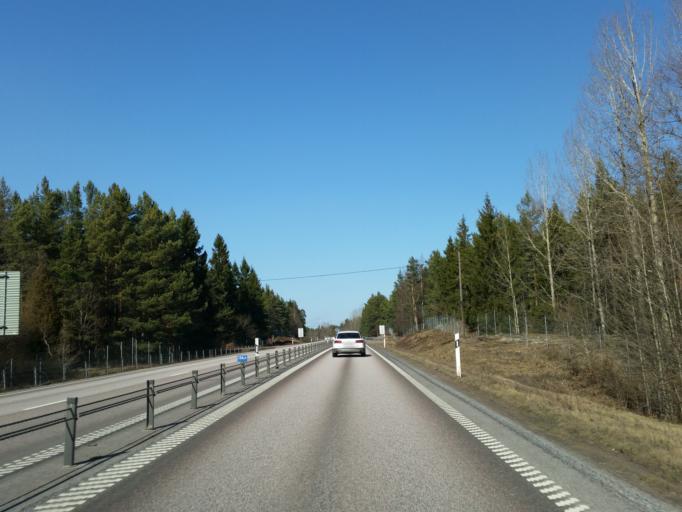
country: SE
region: Kalmar
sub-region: Oskarshamns Kommun
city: Paskallavik
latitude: 57.2011
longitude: 16.4378
